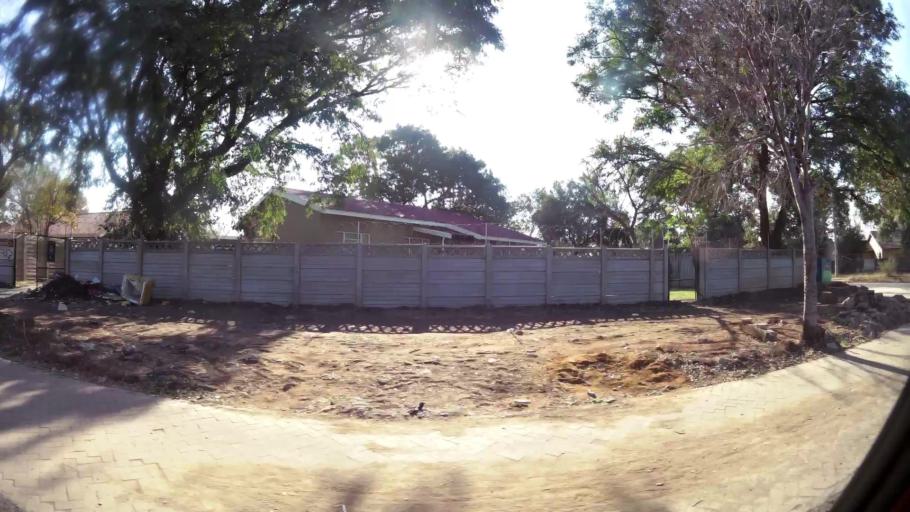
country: ZA
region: North-West
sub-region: Bojanala Platinum District Municipality
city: Rustenburg
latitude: -25.6529
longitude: 27.2387
